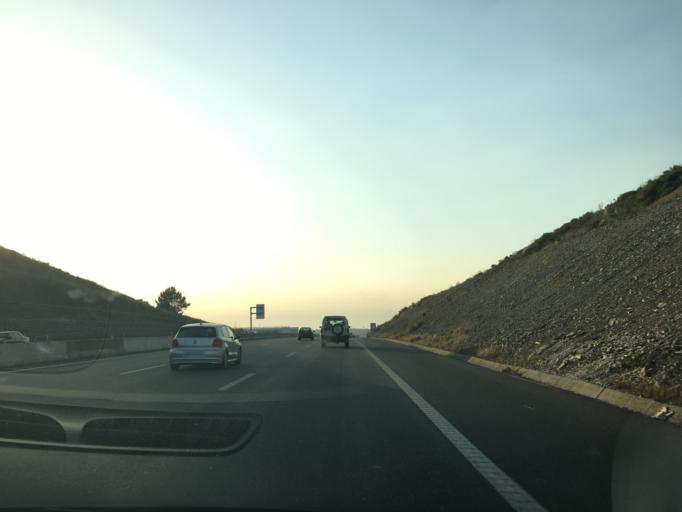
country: PT
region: Lisbon
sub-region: Sintra
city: Sintra
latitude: 38.7965
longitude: -9.3612
